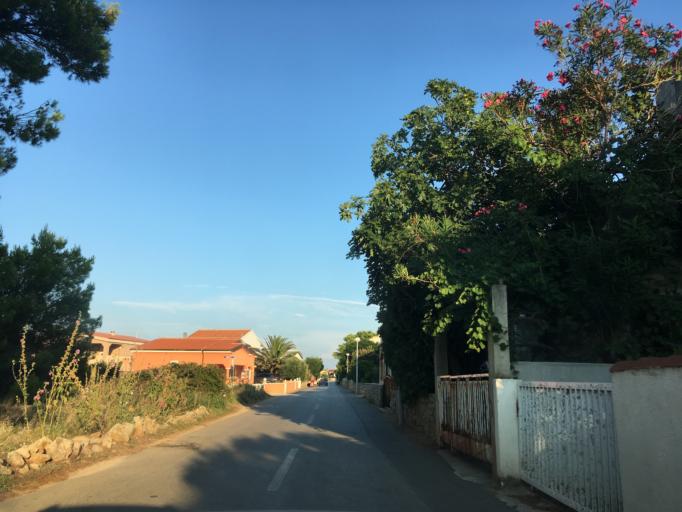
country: HR
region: Zadarska
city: Vir
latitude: 44.3076
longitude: 15.0841
